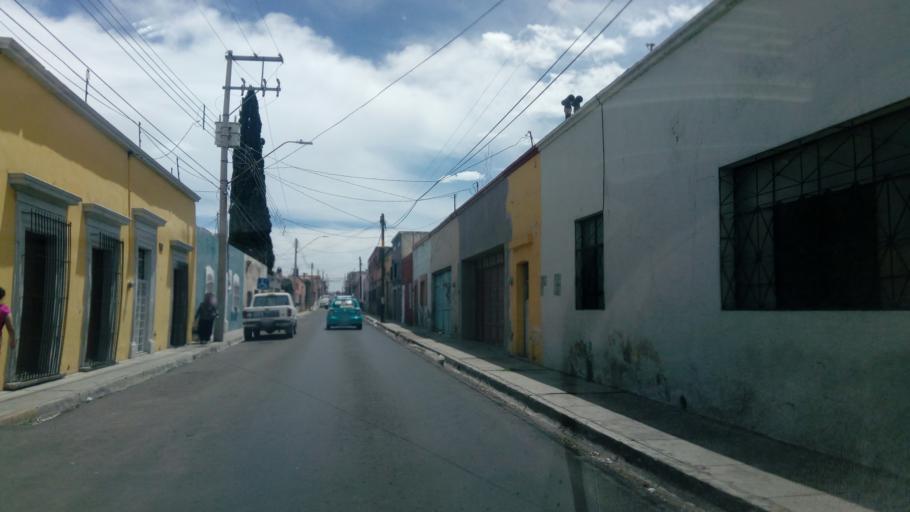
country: MX
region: Durango
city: Victoria de Durango
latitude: 24.0170
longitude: -104.6692
